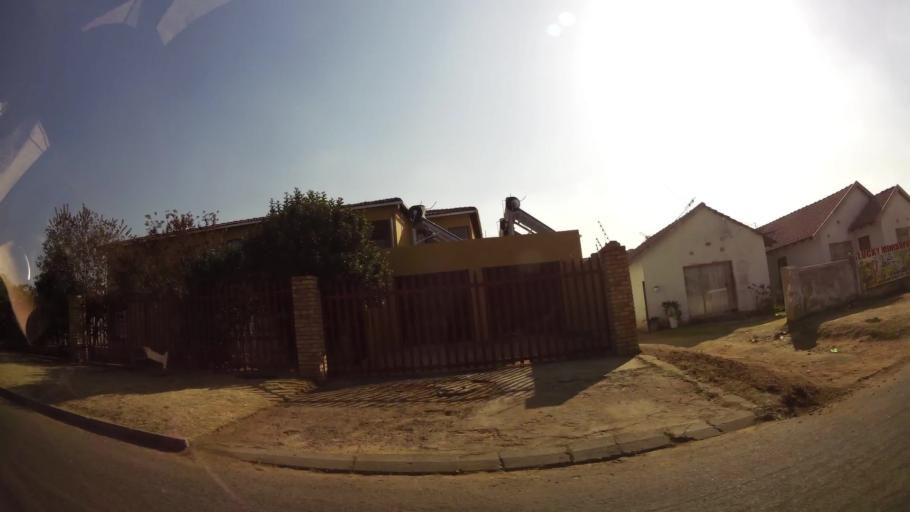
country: ZA
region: Gauteng
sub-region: West Rand District Municipality
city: Randfontein
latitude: -26.1832
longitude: 27.6790
